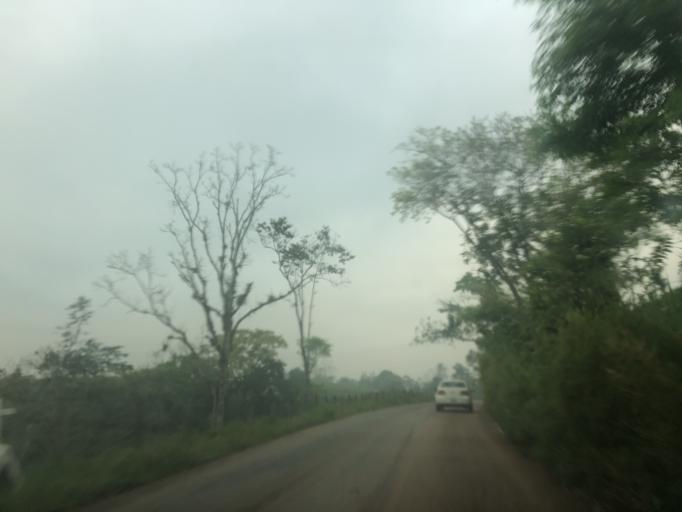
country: MX
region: Chiapas
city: Pueblo Juarez
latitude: 17.6384
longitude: -93.1606
